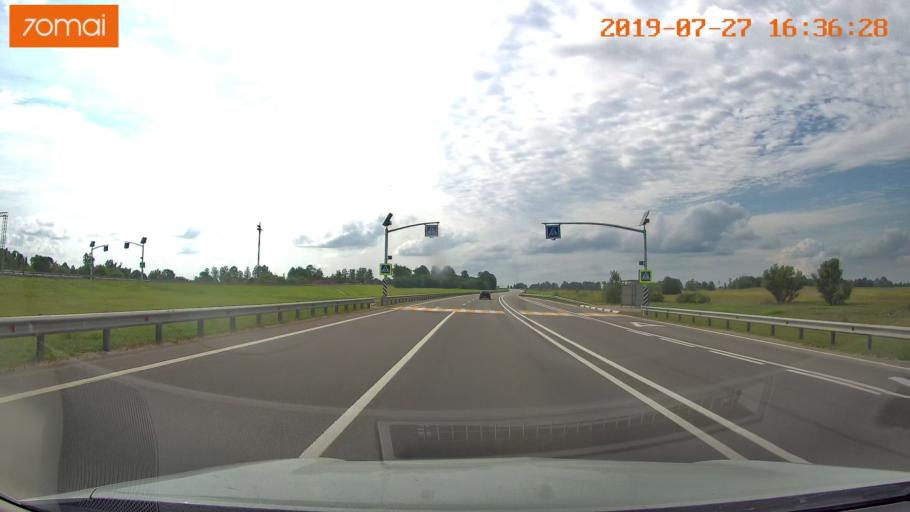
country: RU
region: Kaliningrad
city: Gvardeysk
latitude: 54.6484
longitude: 21.2823
